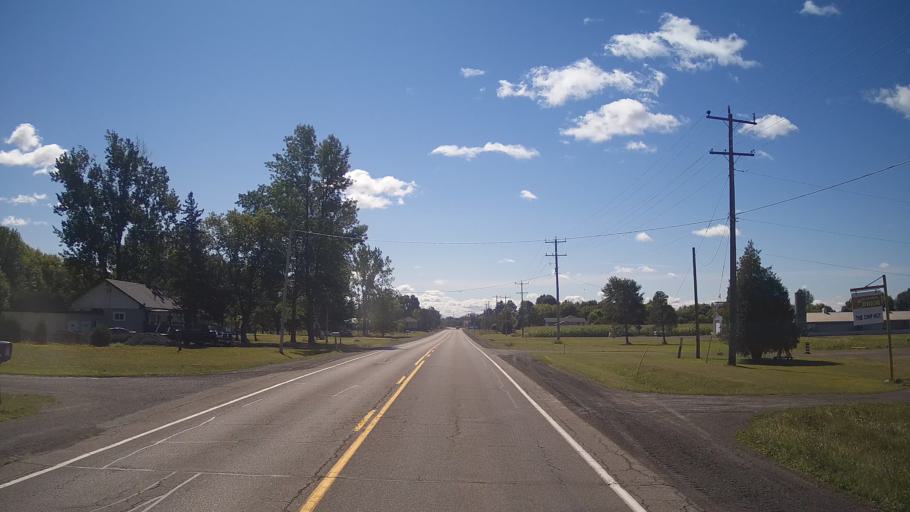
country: US
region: New York
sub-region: St. Lawrence County
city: Norfolk
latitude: 44.9405
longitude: -75.2164
